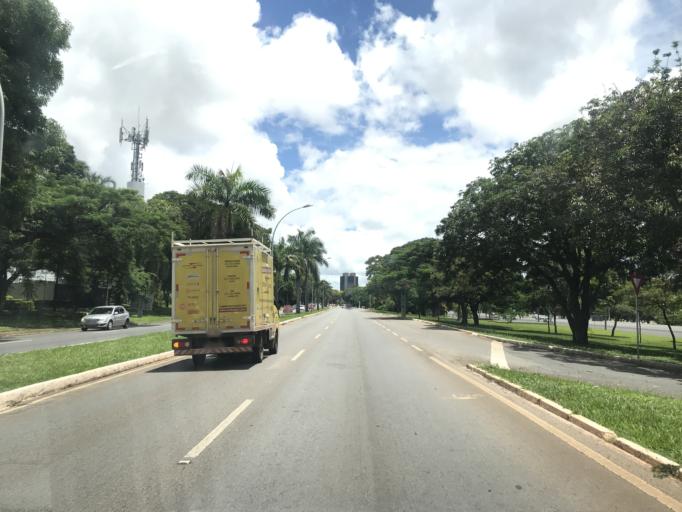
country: BR
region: Federal District
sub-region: Brasilia
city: Brasilia
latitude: -15.8139
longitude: -47.8977
